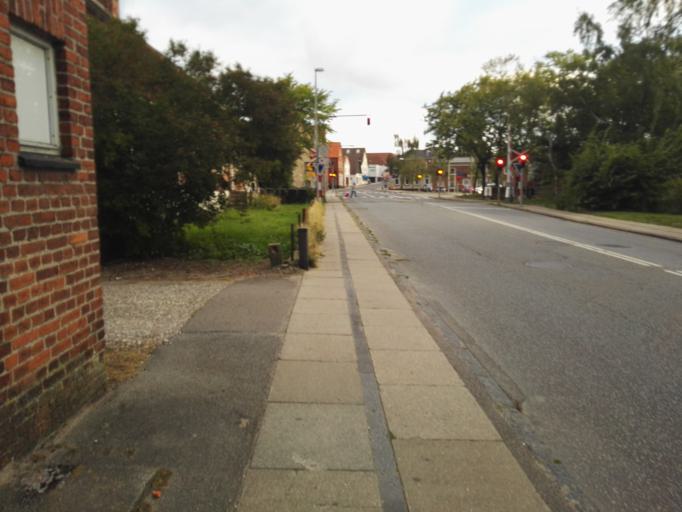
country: DK
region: Zealand
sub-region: Odsherred Kommune
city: Nykobing Sjaelland
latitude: 55.9207
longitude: 11.6723
